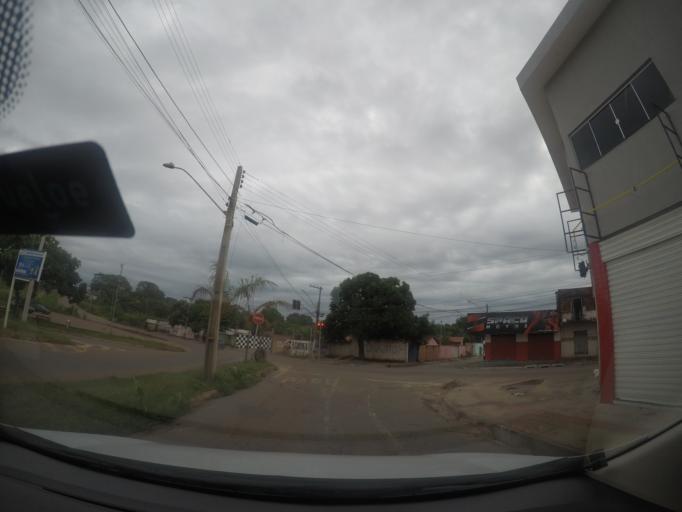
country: BR
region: Goias
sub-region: Goiania
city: Goiania
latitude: -16.6396
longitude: -49.3304
